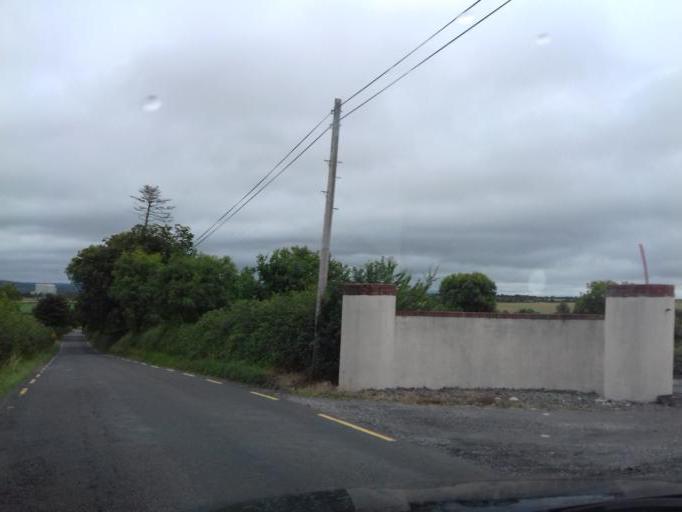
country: IE
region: Leinster
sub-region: County Carlow
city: Bagenalstown
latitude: 52.6223
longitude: -7.0397
